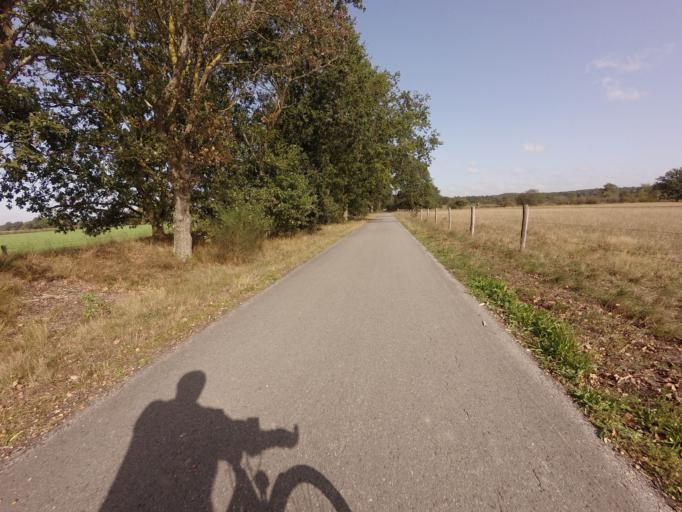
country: NL
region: Limburg
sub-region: Gemeente Roerdalen
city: Herkenbosch
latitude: 51.1889
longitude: 6.0725
